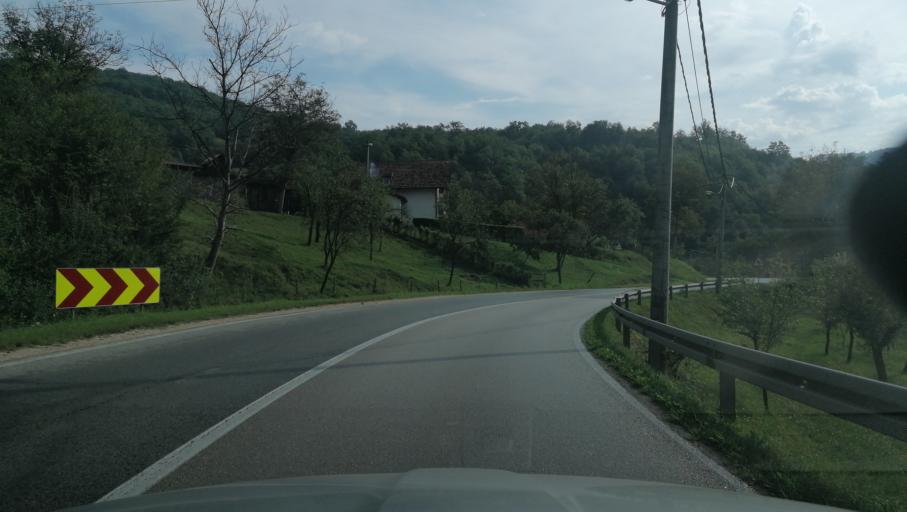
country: BA
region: Republika Srpska
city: Hiseti
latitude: 44.6751
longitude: 17.1471
